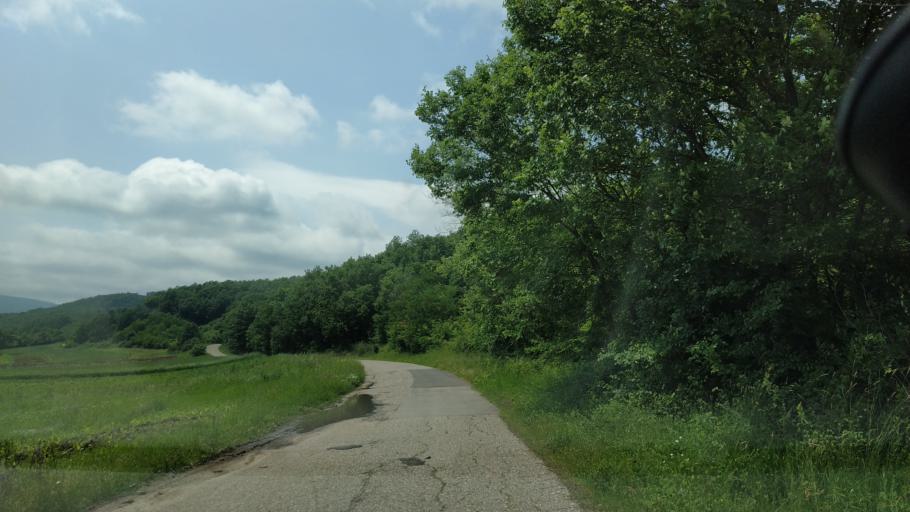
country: RS
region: Central Serbia
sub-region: Nisavski Okrug
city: Aleksinac
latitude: 43.4288
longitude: 21.7332
